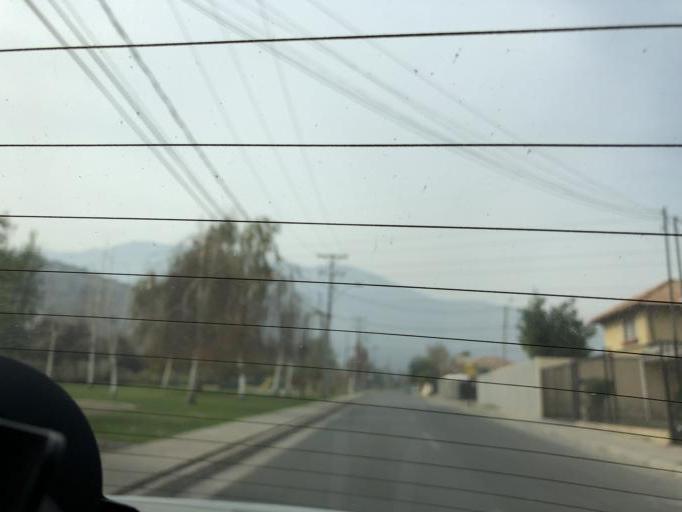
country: CL
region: Santiago Metropolitan
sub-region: Provincia de Cordillera
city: Puente Alto
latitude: -33.5554
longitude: -70.5517
